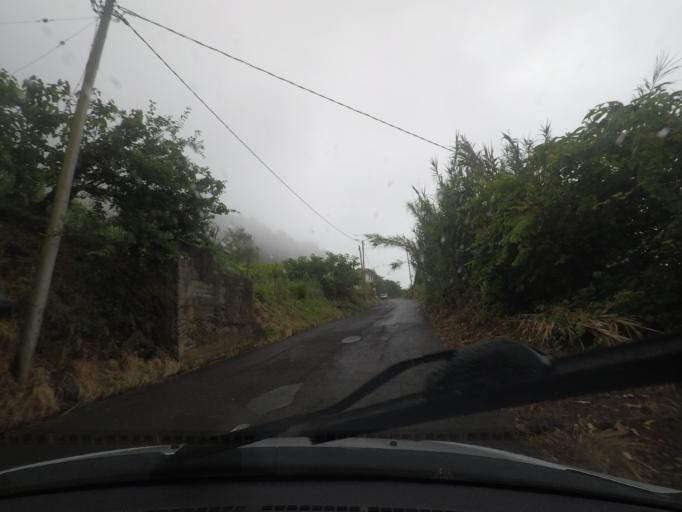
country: PT
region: Madeira
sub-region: Santana
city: Santana
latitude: 32.7754
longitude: -16.8724
